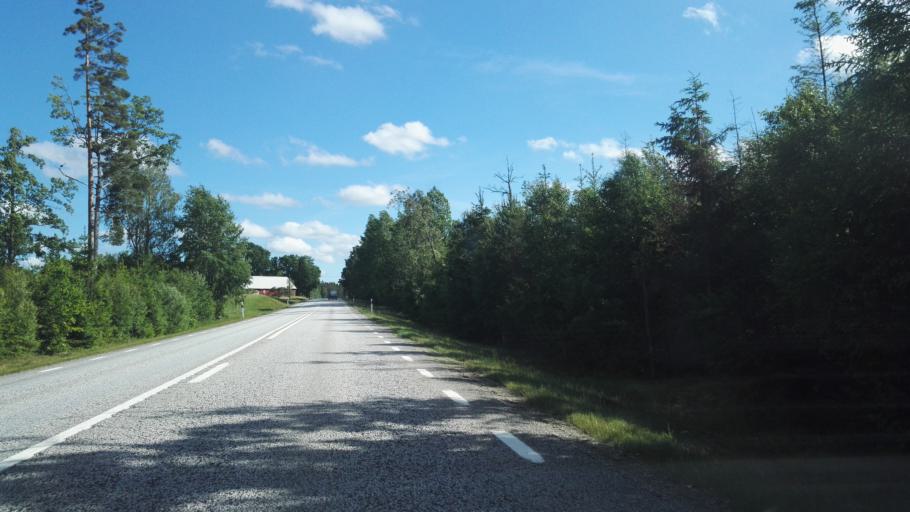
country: SE
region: Joenkoeping
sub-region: Savsjo Kommun
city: Stockaryd
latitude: 57.2947
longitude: 14.5222
